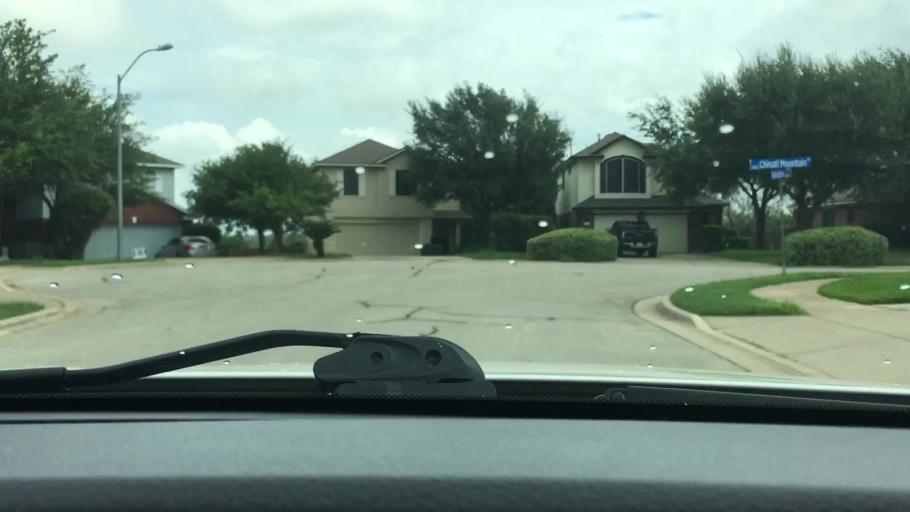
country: US
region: Texas
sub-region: Travis County
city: Windemere
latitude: 30.4751
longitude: -97.6519
